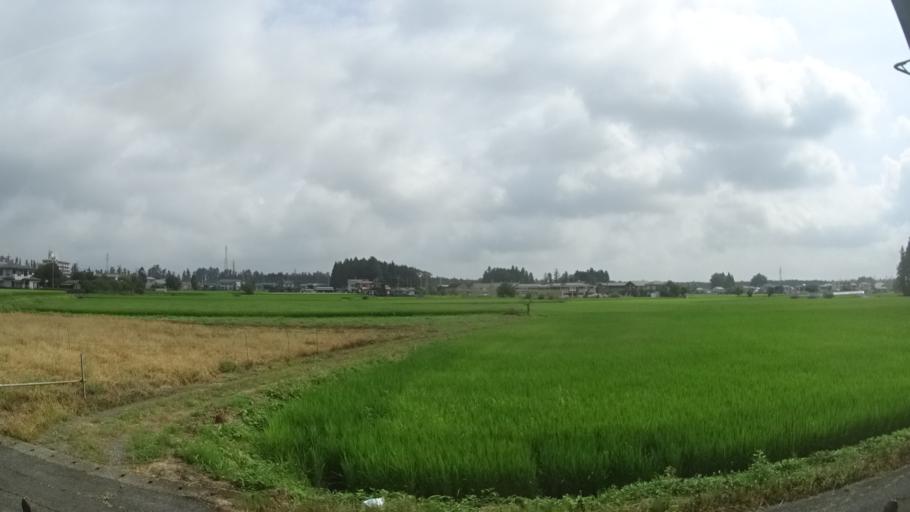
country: JP
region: Tochigi
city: Imaichi
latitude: 36.7124
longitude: 139.6992
